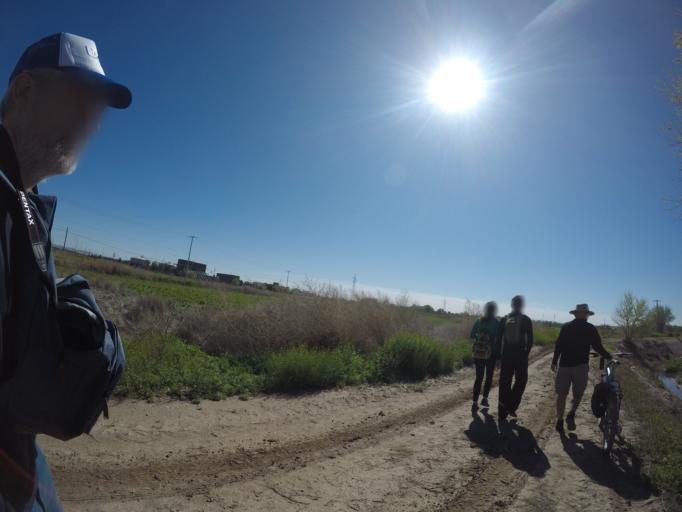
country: US
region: Texas
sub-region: El Paso County
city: Socorro
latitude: 31.6422
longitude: -106.3356
